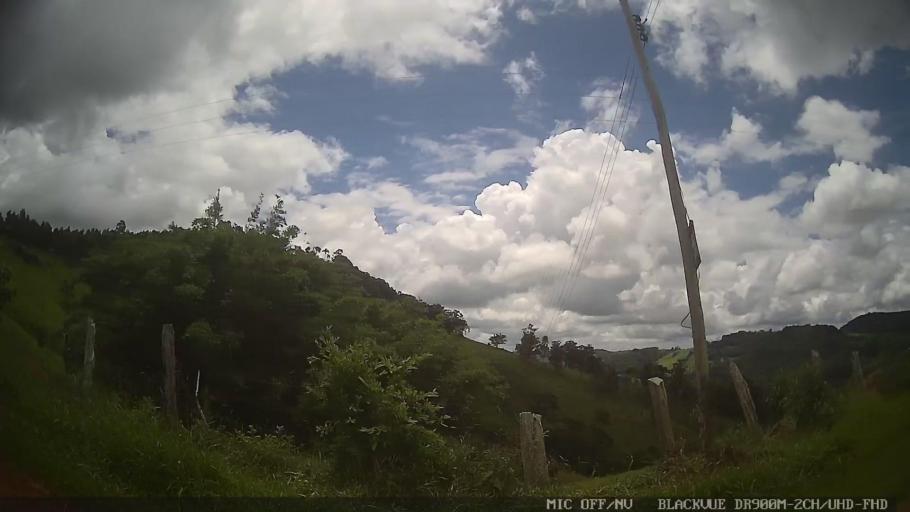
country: BR
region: Minas Gerais
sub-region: Extrema
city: Extrema
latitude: -22.7830
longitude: -46.4536
